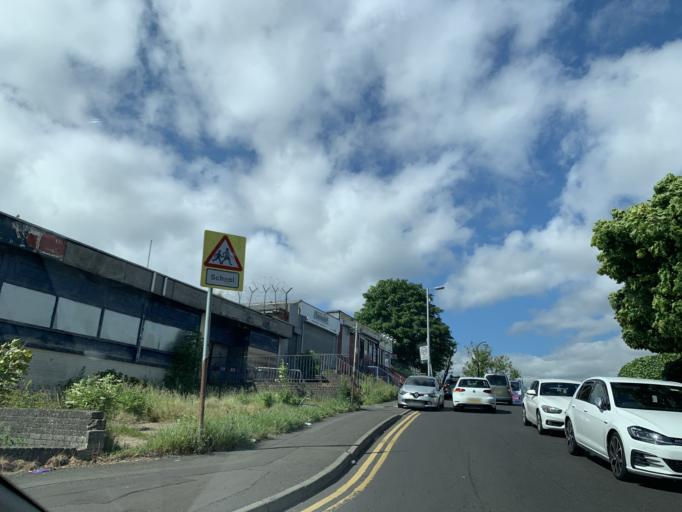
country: GB
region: Scotland
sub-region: East Renfrewshire
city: Newton Mearns
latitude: 55.8055
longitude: -4.3324
